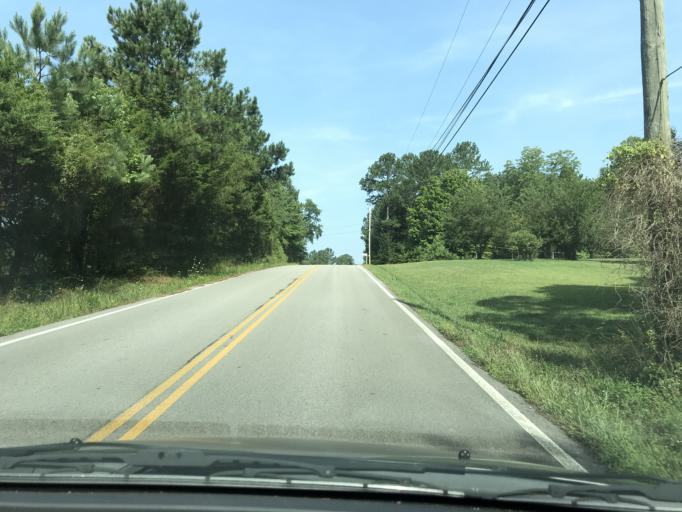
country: US
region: Tennessee
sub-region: Hamilton County
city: Apison
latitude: 35.0538
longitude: -85.0025
